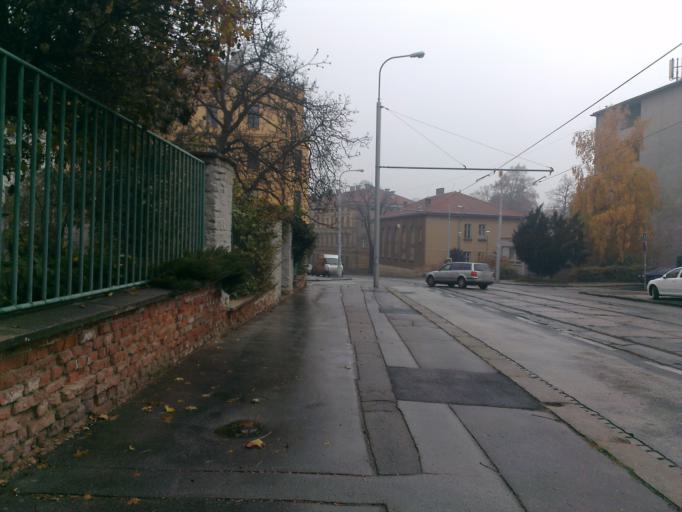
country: CZ
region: South Moravian
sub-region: Mesto Brno
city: Brno
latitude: 49.1986
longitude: 16.5902
